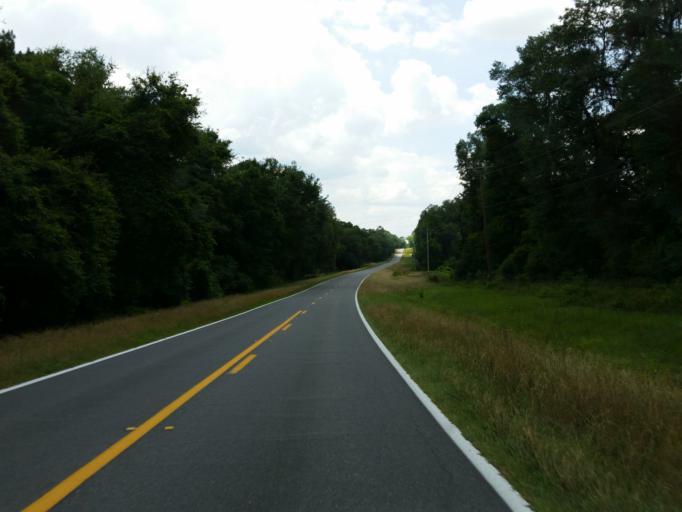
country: US
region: Florida
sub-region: Alachua County
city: High Springs
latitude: 29.9526
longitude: -82.5945
